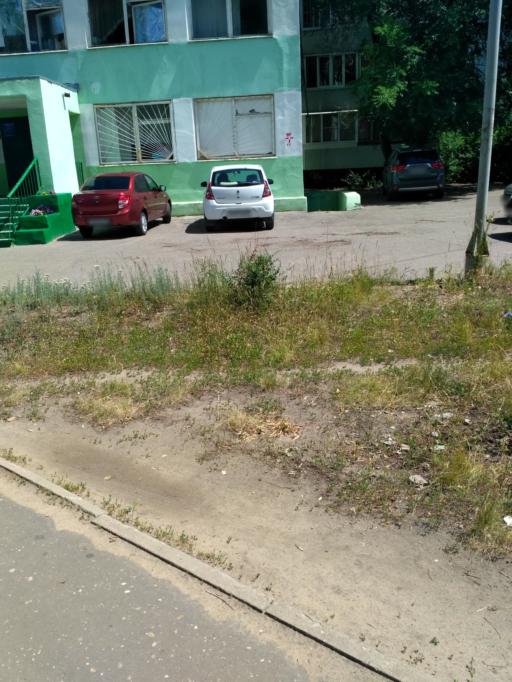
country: RU
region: Voronezj
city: Voronezh
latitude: 51.6493
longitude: 39.1390
